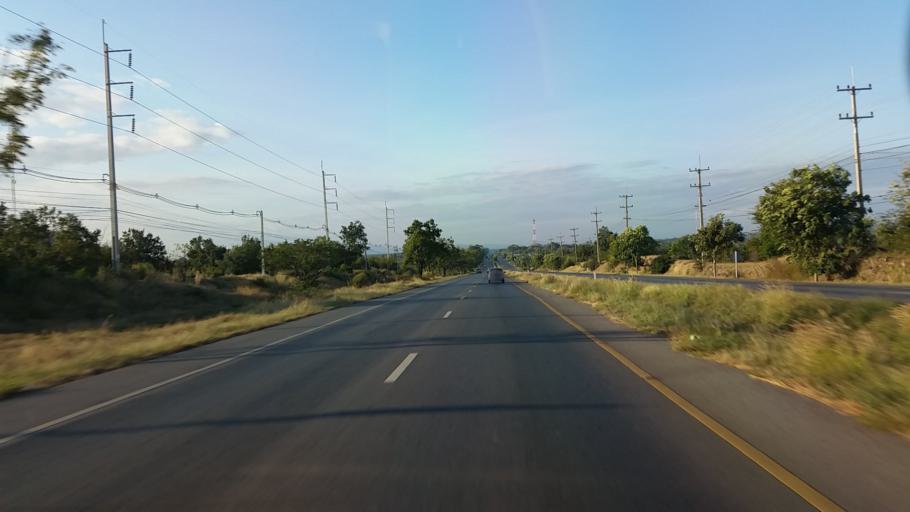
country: TH
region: Lop Buri
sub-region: Amphoe Tha Luang
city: Tha Luang
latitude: 15.1326
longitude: 101.0408
